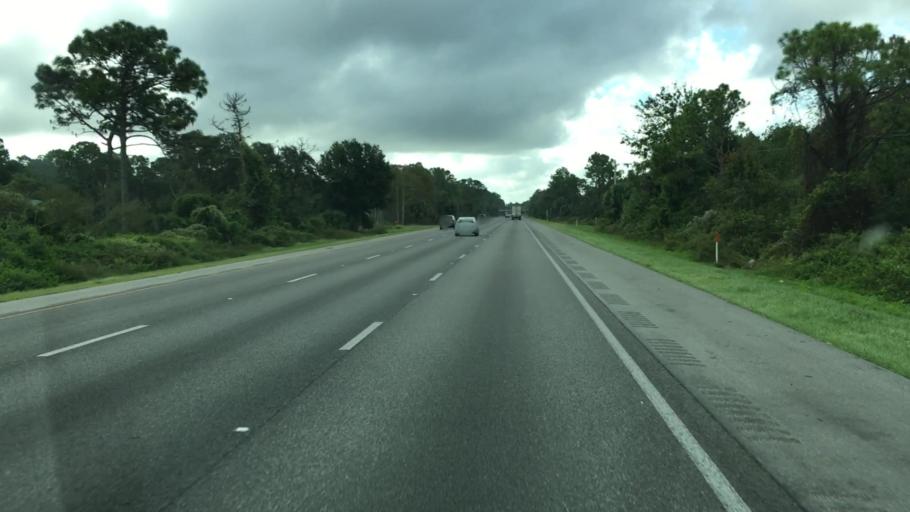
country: US
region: Florida
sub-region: Volusia County
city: Glencoe
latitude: 29.0572
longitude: -81.0082
